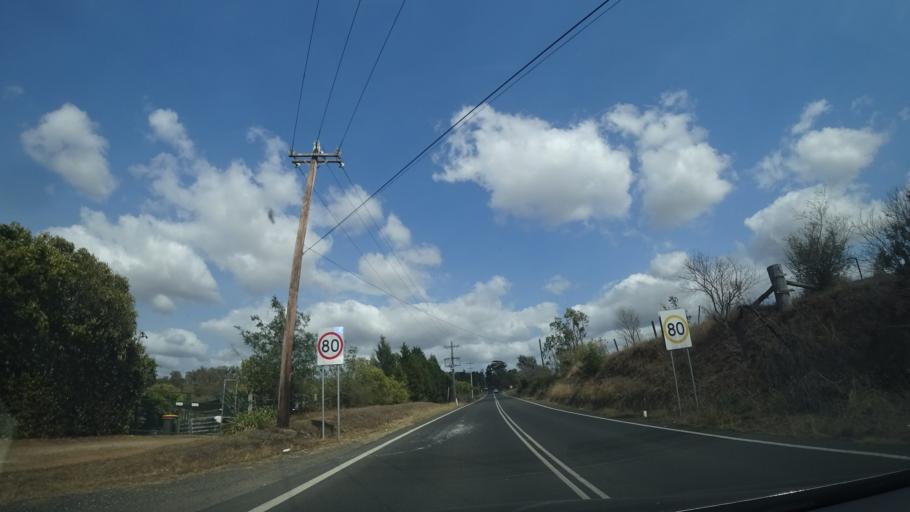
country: AU
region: New South Wales
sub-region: Wollondilly
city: Picton
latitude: -34.1870
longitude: 150.6020
